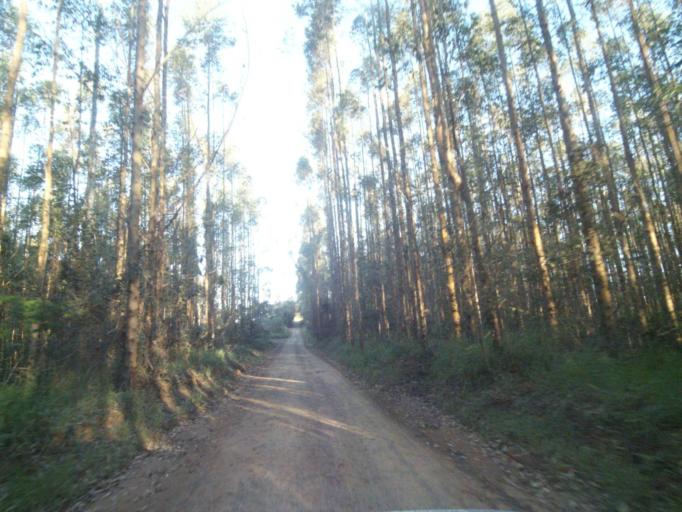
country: BR
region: Parana
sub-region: Telemaco Borba
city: Telemaco Borba
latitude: -24.4969
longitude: -50.6004
